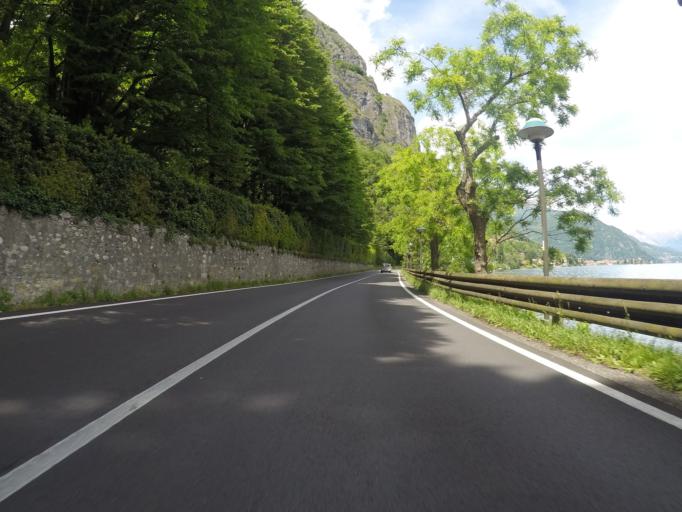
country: IT
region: Lombardy
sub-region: Provincia di Como
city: Griante
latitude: 46.0022
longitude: 9.2349
